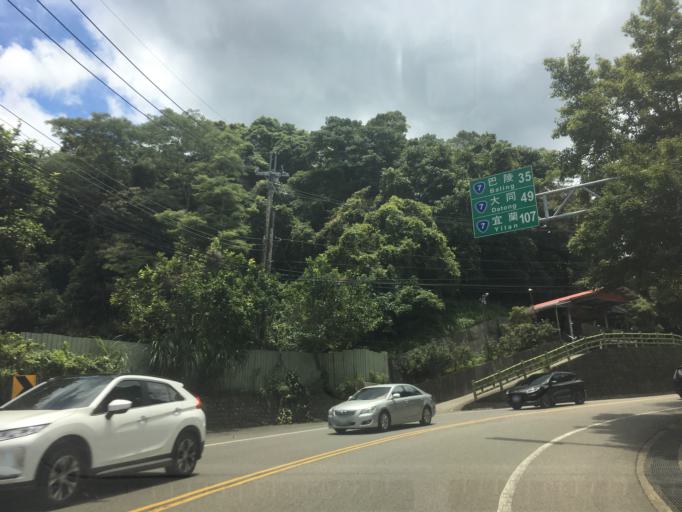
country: TW
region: Taiwan
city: Daxi
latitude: 24.8304
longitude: 121.3340
